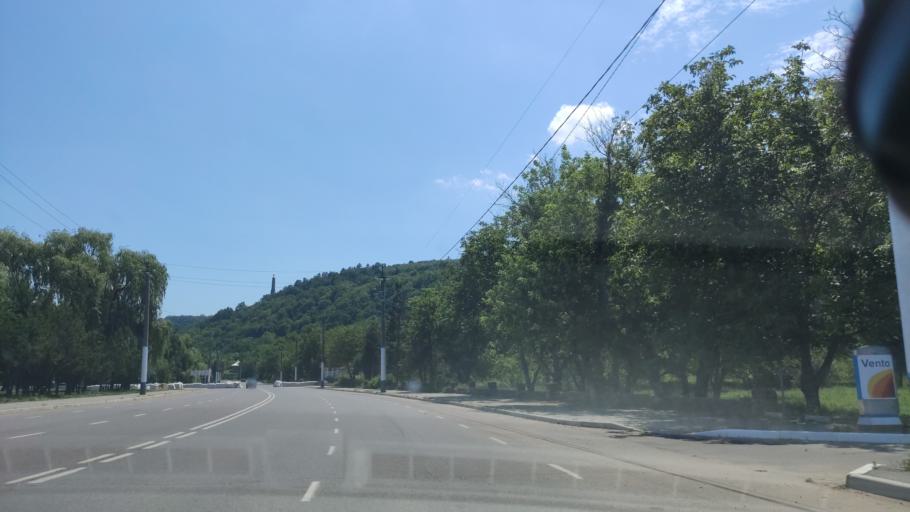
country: MD
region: Raionul Soroca
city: Soroca
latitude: 48.1443
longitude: 28.3021
